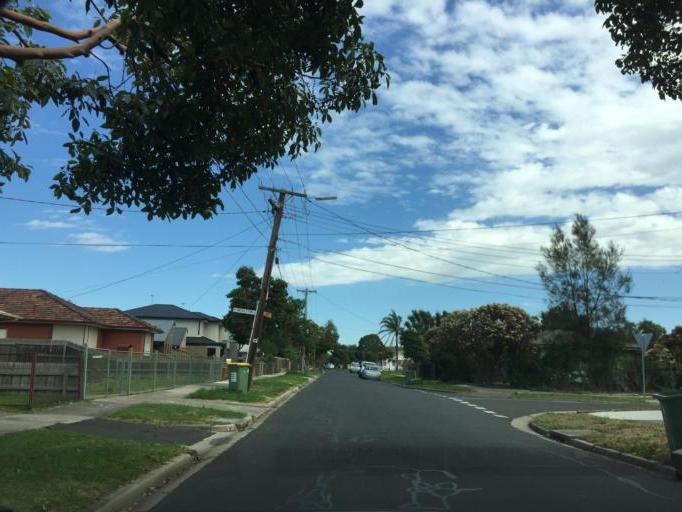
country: AU
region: Victoria
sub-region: Maribyrnong
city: Braybrook
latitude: -37.7857
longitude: 144.8627
